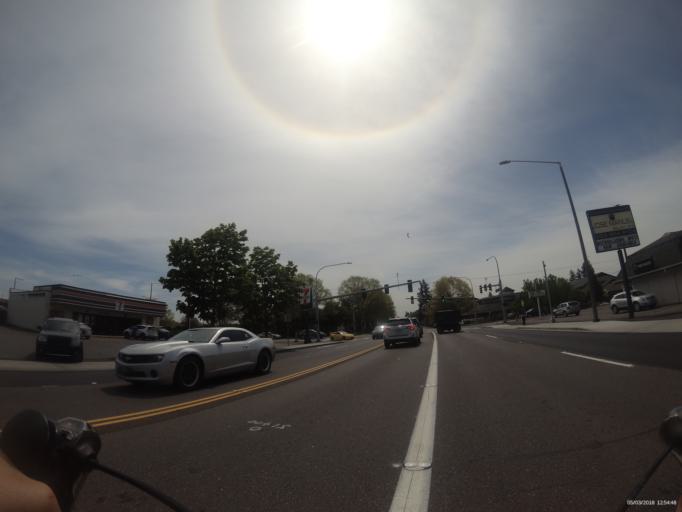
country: US
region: Washington
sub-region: Pierce County
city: Lakewood
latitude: 47.1672
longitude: -122.5207
